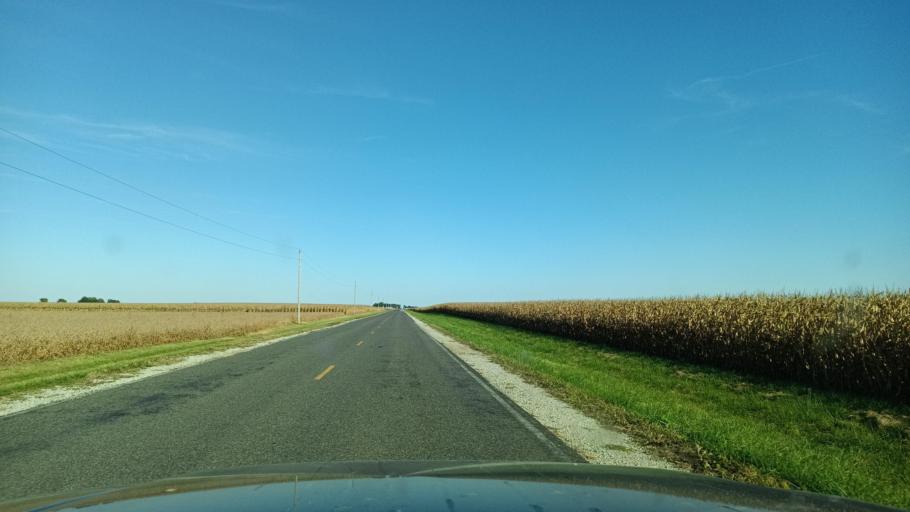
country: US
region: Illinois
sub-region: De Witt County
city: Clinton
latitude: 40.2244
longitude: -88.9443
